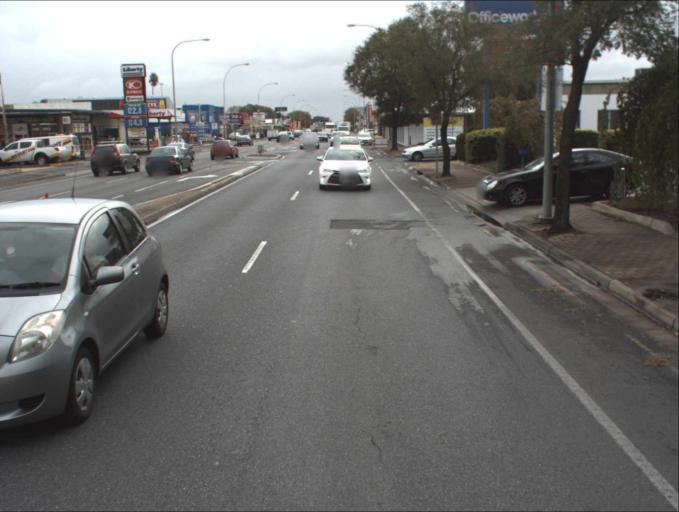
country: AU
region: South Australia
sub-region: Prospect
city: Prospect
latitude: -34.8892
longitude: 138.6031
